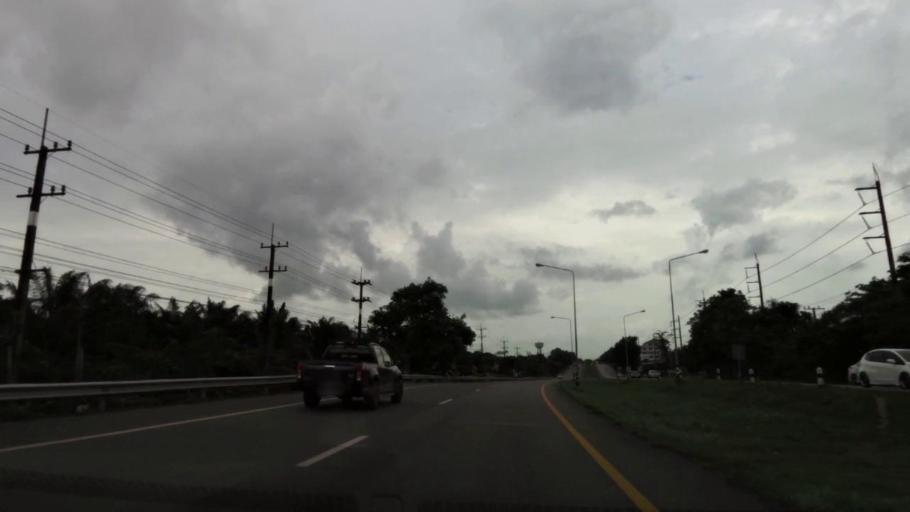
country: TH
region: Chanthaburi
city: Tha Mai
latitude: 12.7000
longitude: 101.9863
